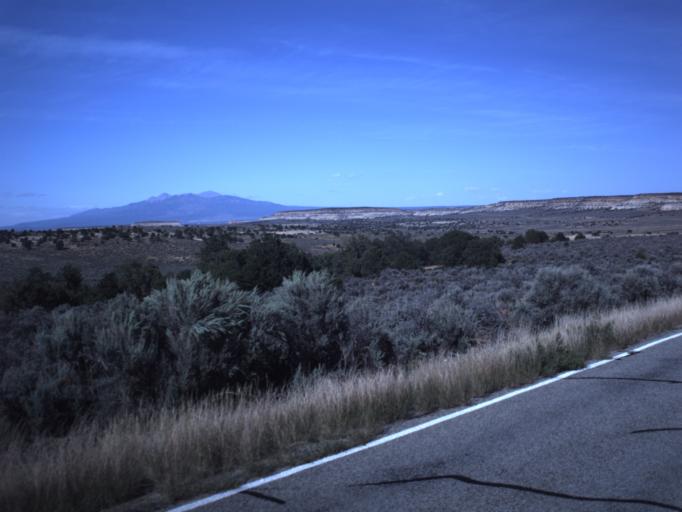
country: US
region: Utah
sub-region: San Juan County
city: Monticello
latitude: 38.0045
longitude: -109.4536
